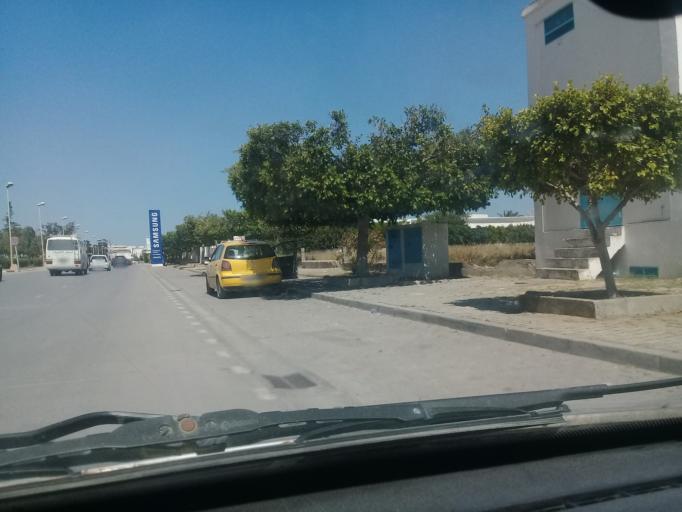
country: TN
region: Ariana
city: Ariana
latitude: 36.8329
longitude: 10.2216
